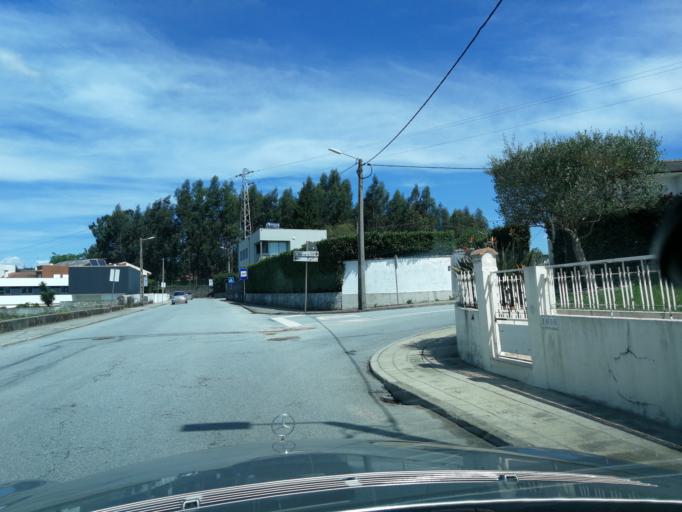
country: PT
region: Braga
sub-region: Vila Nova de Famalicao
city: Vila Nova de Famalicao
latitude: 41.4190
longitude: -8.5137
